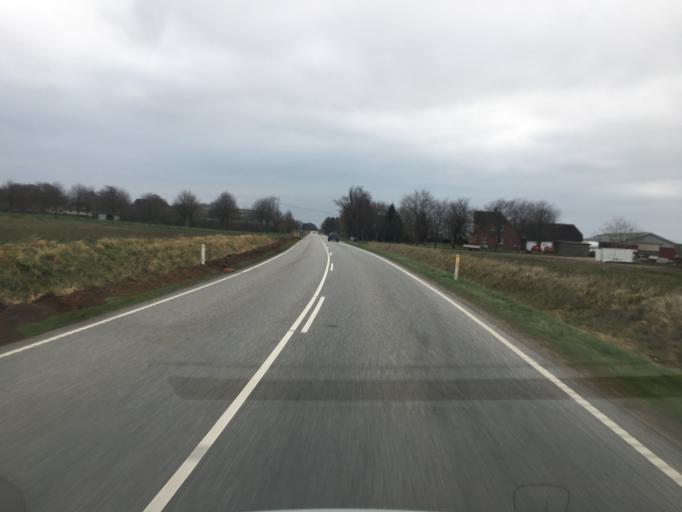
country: DK
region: South Denmark
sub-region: Aabenraa Kommune
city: Rodekro
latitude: 55.0177
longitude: 9.2940
